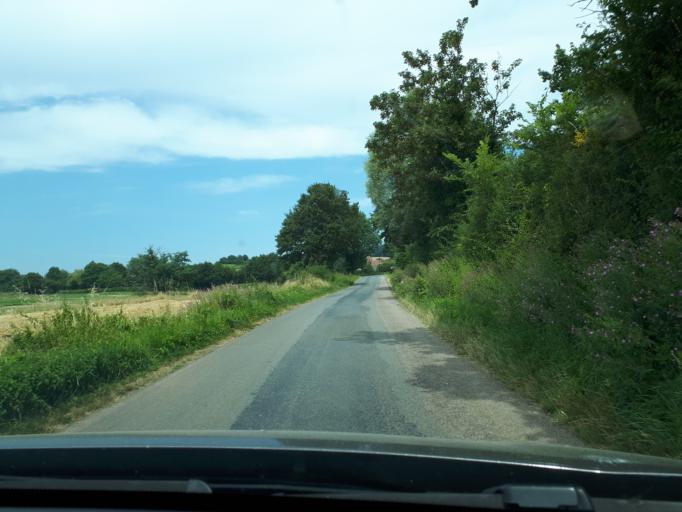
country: FR
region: Centre
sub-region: Departement du Cher
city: Sancerre
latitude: 47.3019
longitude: 2.7465
